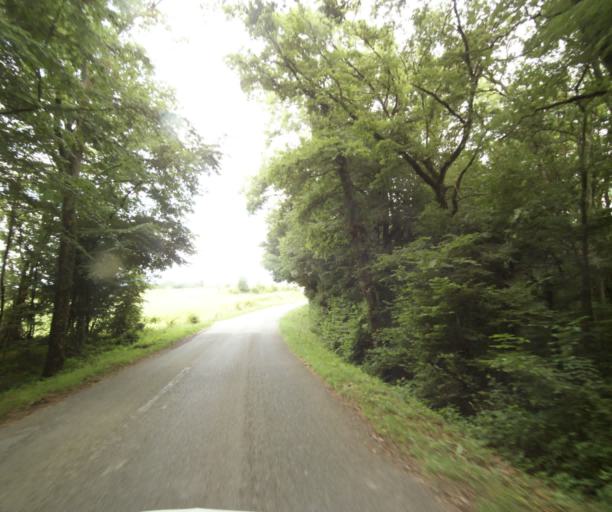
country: FR
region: Rhone-Alpes
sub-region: Departement de la Haute-Savoie
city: Allinges
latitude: 46.3457
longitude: 6.4545
